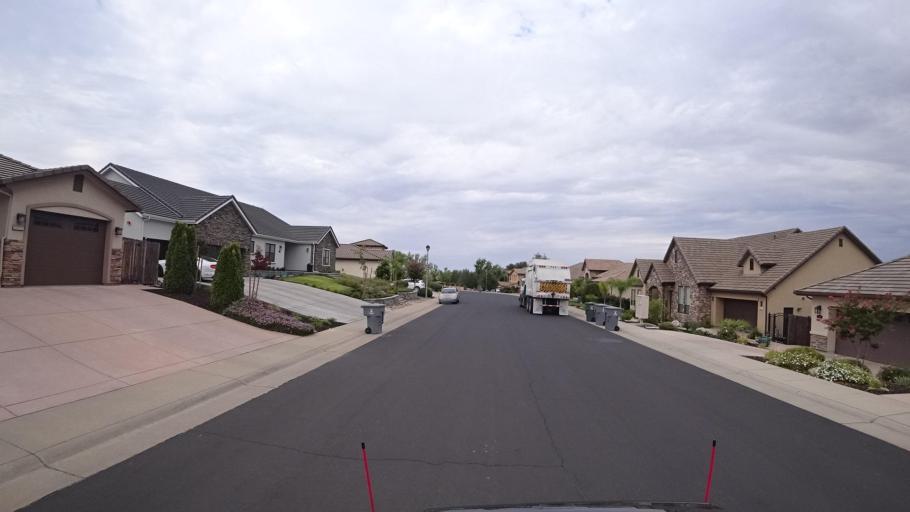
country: US
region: California
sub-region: Placer County
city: Rocklin
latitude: 38.7730
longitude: -121.2332
